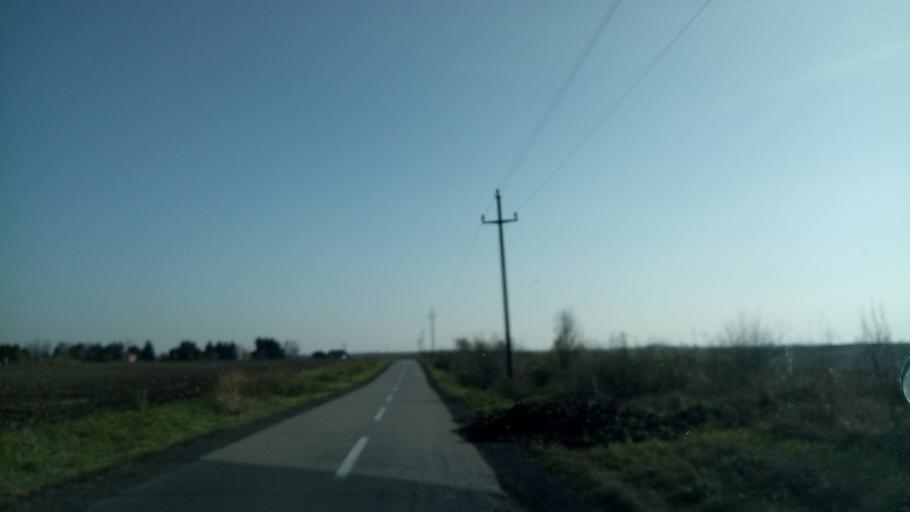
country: RS
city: Ljukovo
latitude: 45.0323
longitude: 20.0456
